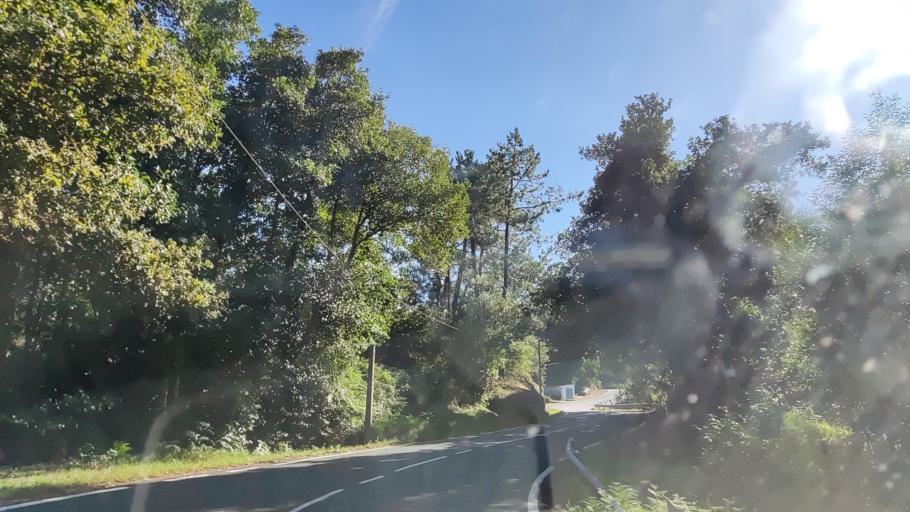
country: ES
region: Galicia
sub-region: Provincia da Coruna
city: Boiro
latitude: 42.5725
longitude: -9.0027
